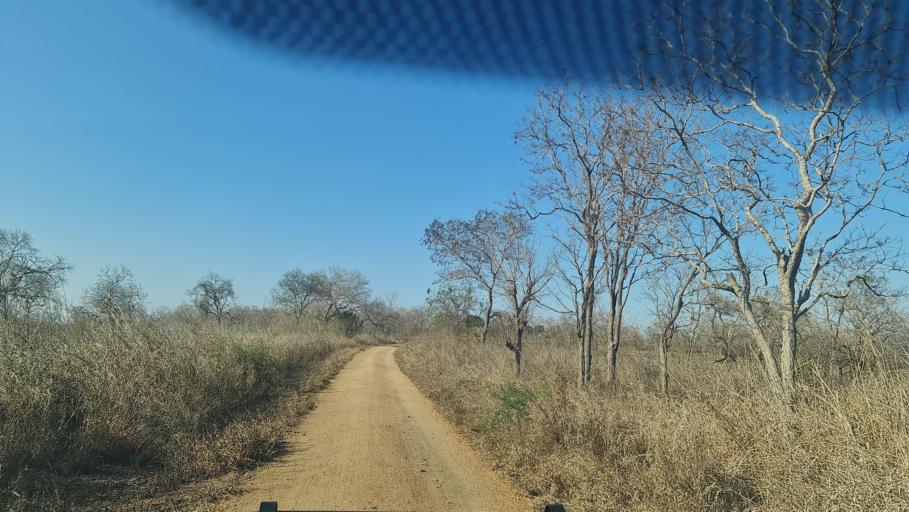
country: MZ
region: Nampula
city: Nacala
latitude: -13.9467
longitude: 40.4792
